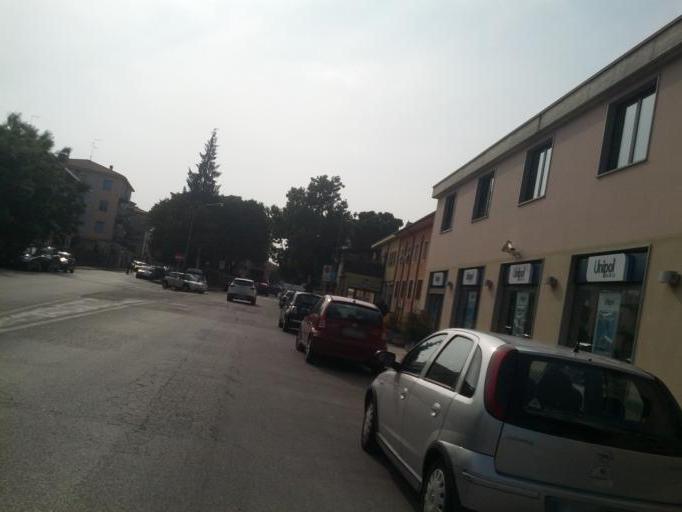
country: IT
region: Veneto
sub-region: Provincia di Verona
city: Poiano
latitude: 45.4398
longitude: 11.0302
